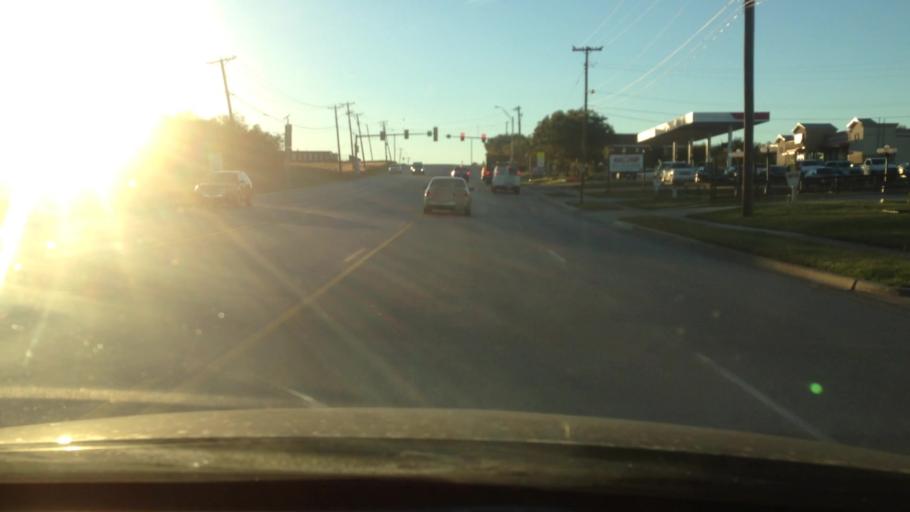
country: US
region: Texas
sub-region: Tarrant County
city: Watauga
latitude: 32.8606
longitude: -97.2524
